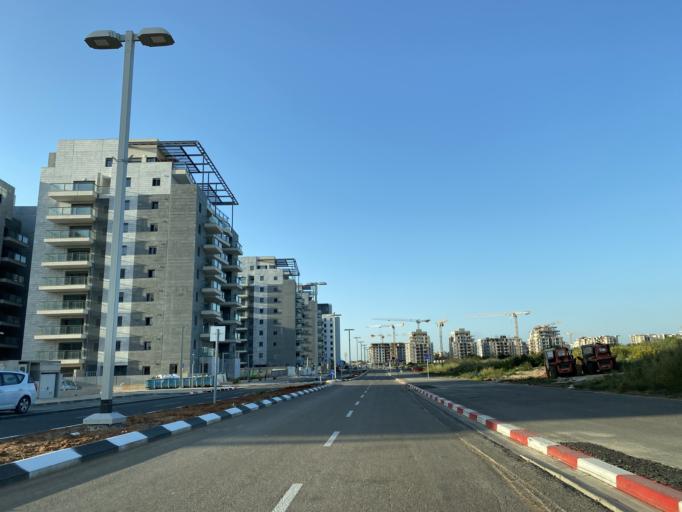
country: IL
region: Tel Aviv
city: Herzliyya
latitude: 32.1565
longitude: 34.8223
